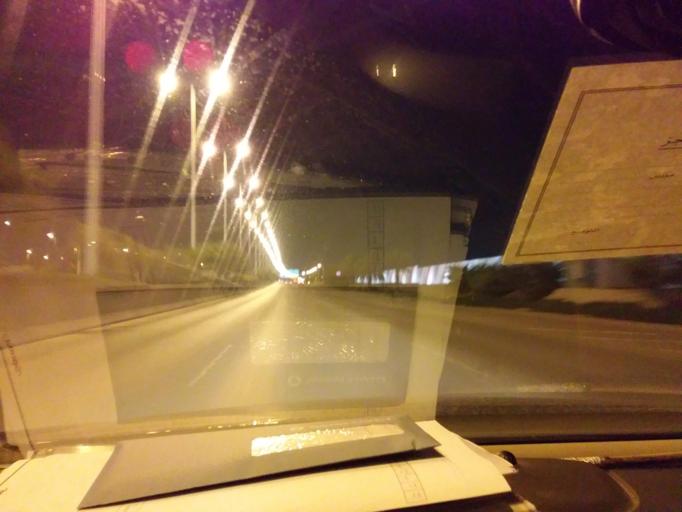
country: SA
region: Ar Riyad
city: Riyadh
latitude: 24.7236
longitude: 46.7001
